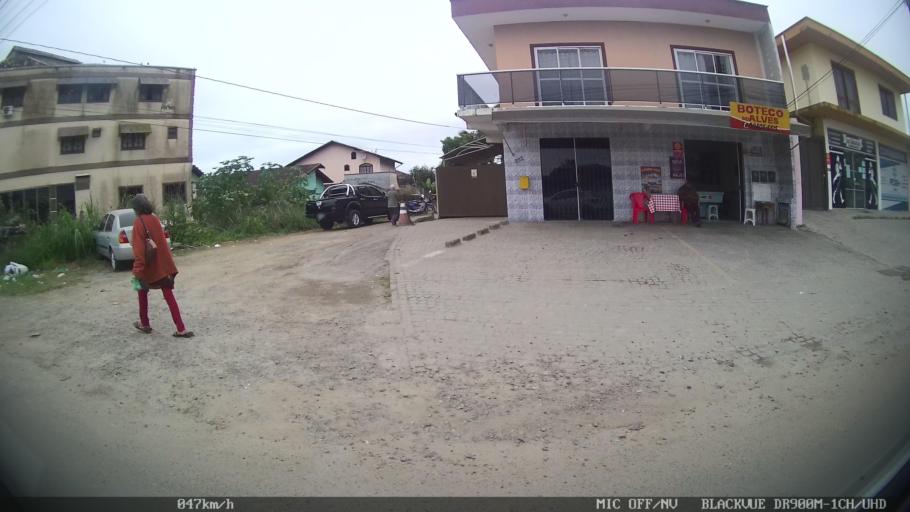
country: BR
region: Santa Catarina
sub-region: Joinville
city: Joinville
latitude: -26.3364
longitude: -48.8169
